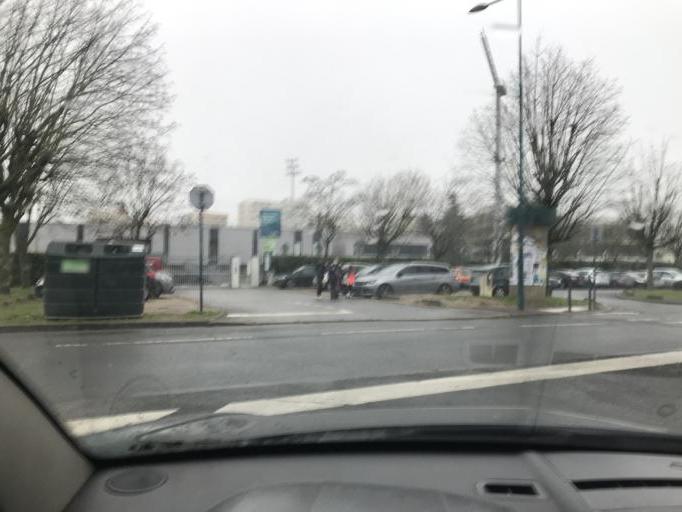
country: FR
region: Ile-de-France
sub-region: Departement du Val-d'Oise
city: Cergy-Pontoise
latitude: 49.0347
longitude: 2.0871
